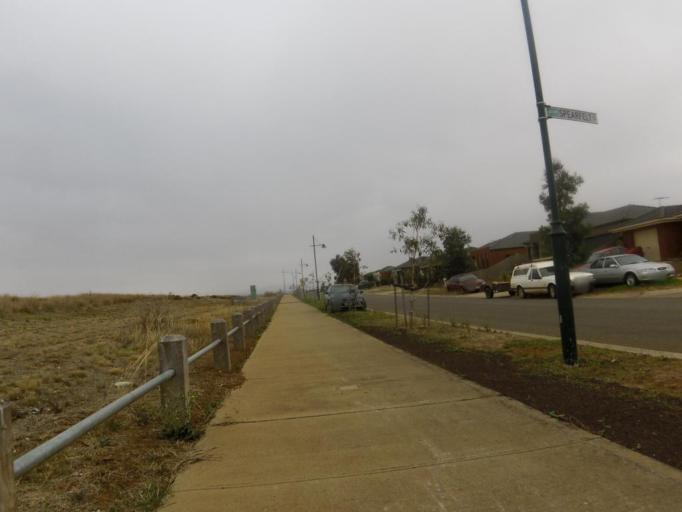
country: AU
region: Victoria
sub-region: Melton
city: Kurunjang
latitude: -37.6553
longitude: 144.5880
